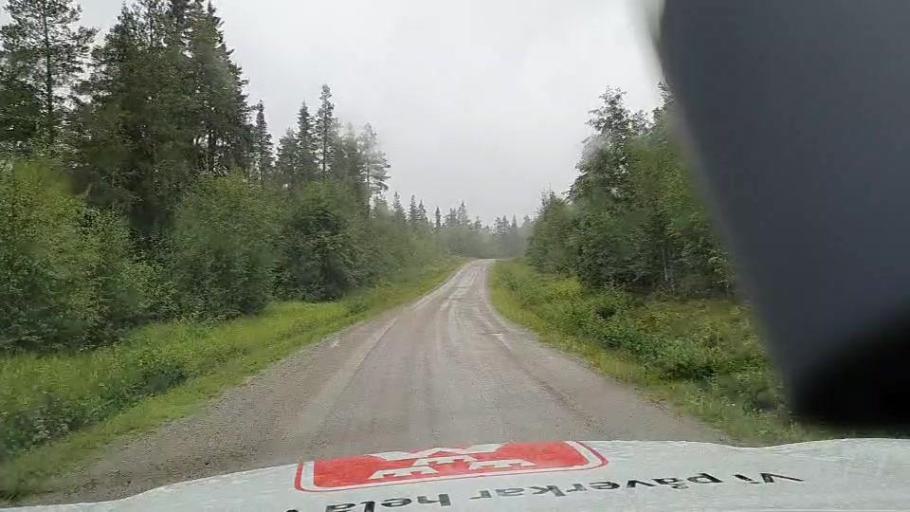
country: SE
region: Jaemtland
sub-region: OEstersunds Kommun
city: Brunflo
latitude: 62.8430
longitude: 15.0213
